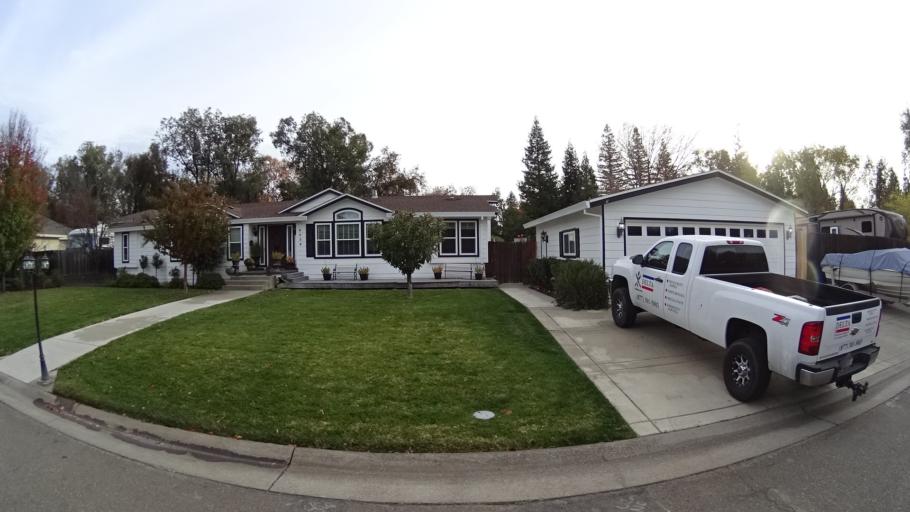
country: US
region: California
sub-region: Sacramento County
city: Citrus Heights
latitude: 38.7123
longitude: -121.2749
